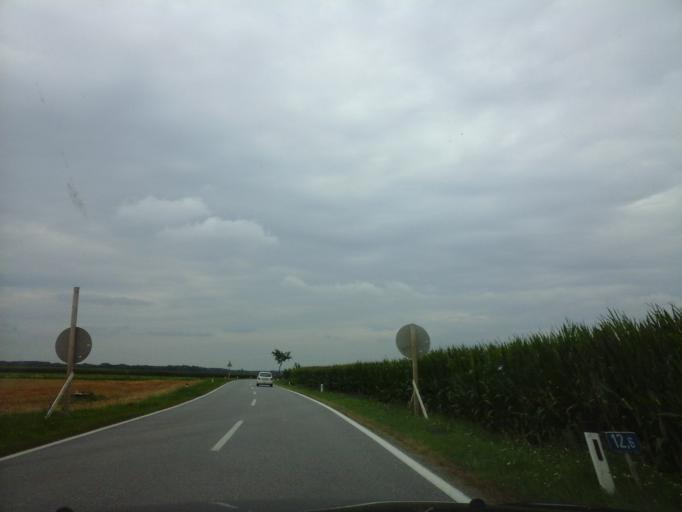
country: AT
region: Lower Austria
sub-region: Politischer Bezirk Ganserndorf
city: Orth an der Donau
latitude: 48.1558
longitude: 16.7367
